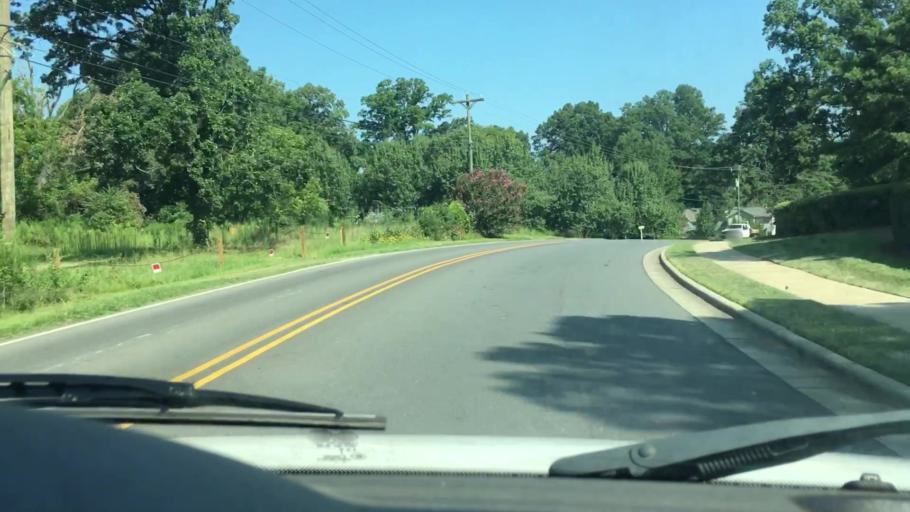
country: US
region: North Carolina
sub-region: Mecklenburg County
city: Charlotte
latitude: 35.3160
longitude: -80.8524
